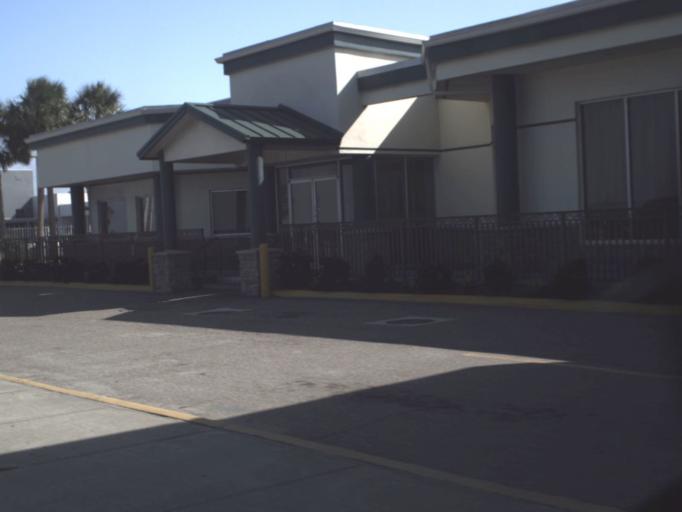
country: US
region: Florida
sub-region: Brevard County
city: Melbourne
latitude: 28.1030
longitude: -80.6148
